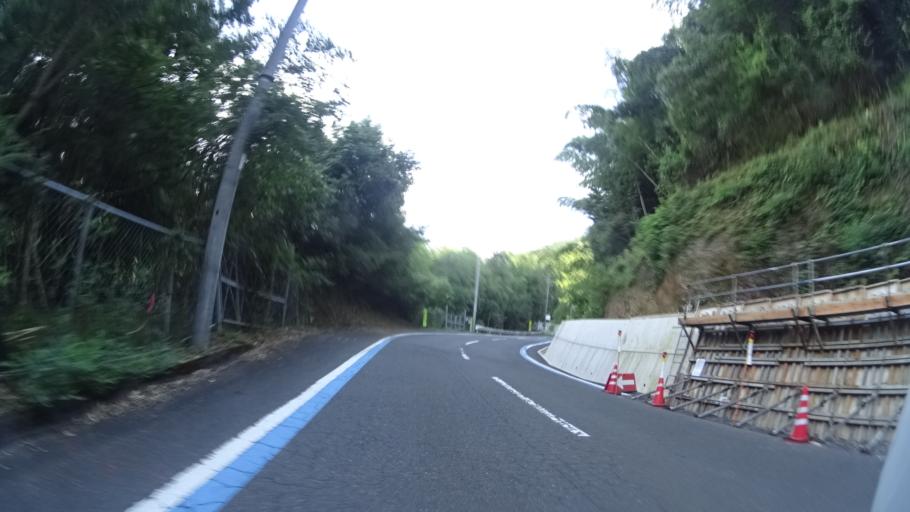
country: JP
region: Kyoto
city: Maizuru
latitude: 35.4428
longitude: 135.3941
